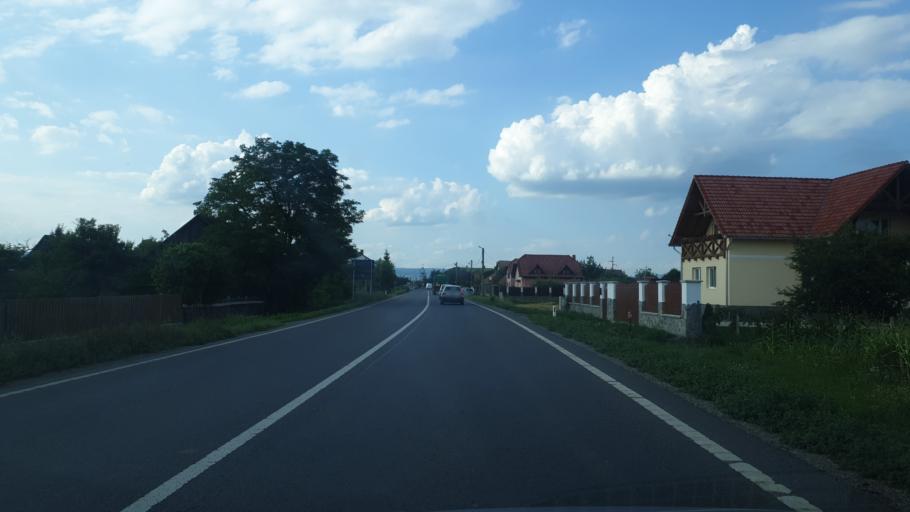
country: RO
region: Covasna
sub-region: Municipiul Sfantu Gheorghe
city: Sfantu-Gheorghe
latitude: 45.8336
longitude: 25.8046
